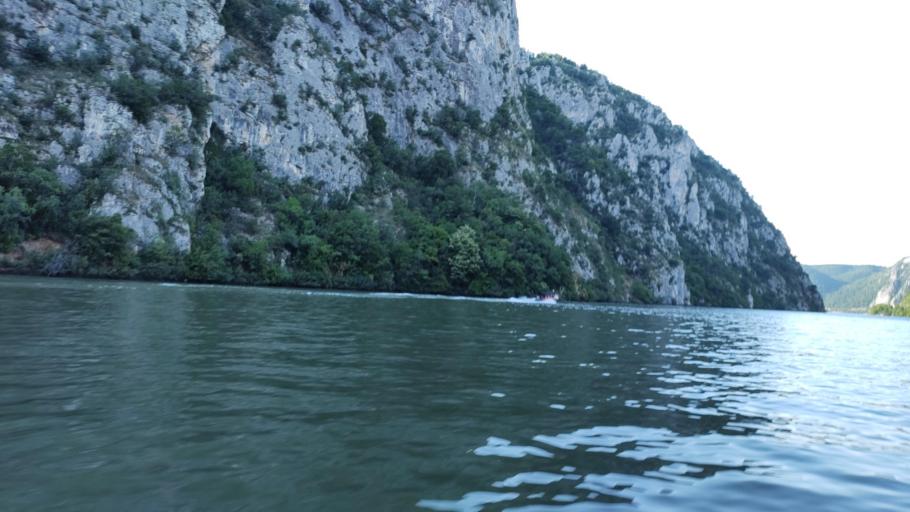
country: RO
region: Mehedinti
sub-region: Comuna Dubova
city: Dubova
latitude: 44.6076
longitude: 22.2693
